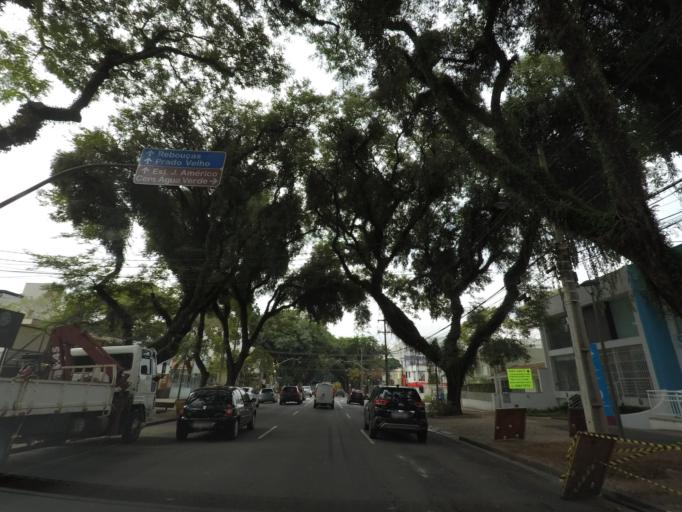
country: BR
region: Parana
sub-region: Curitiba
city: Curitiba
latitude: -25.4484
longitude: -49.2809
